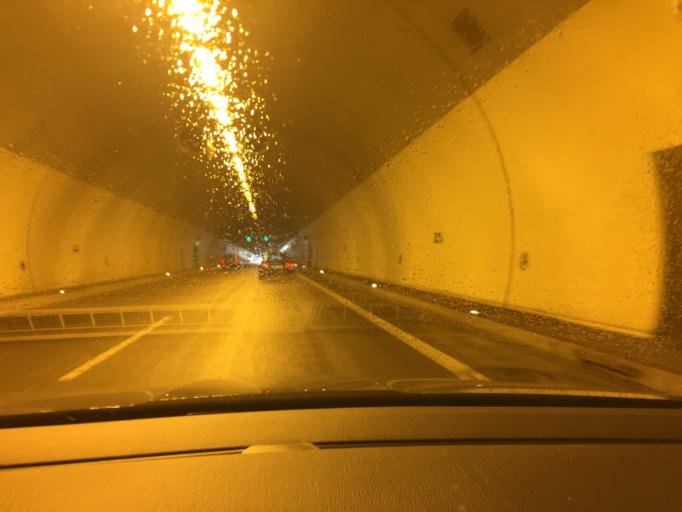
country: CZ
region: Ustecky
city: Velemin
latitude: 50.5815
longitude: 14.0118
